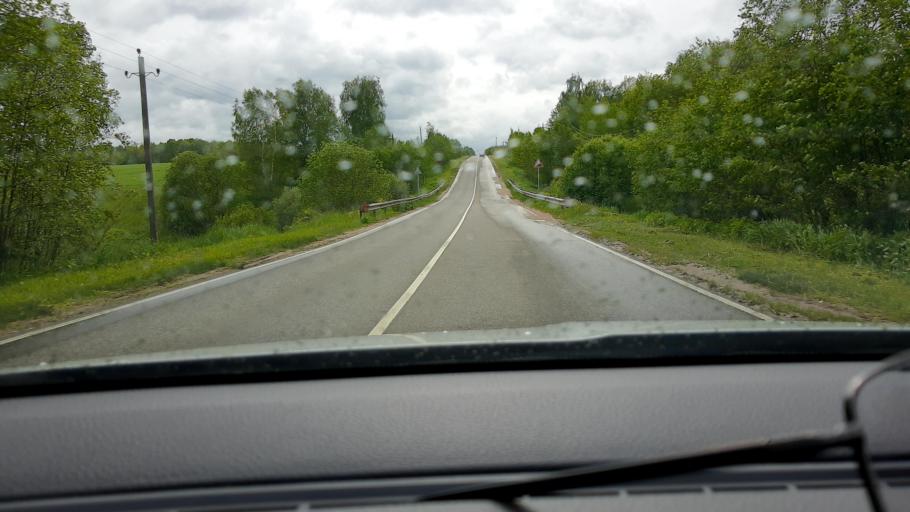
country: RU
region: Moskovskaya
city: Yershovo
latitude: 55.7573
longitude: 36.9500
